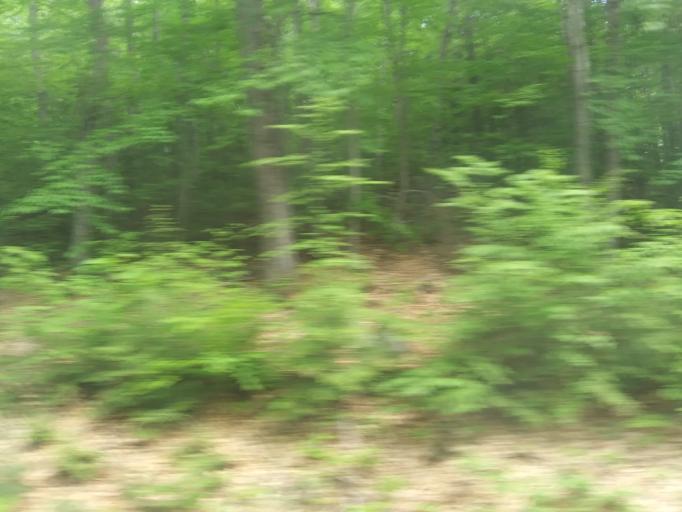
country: US
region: Massachusetts
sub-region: Franklin County
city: Buckland
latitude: 42.5725
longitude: -72.7619
